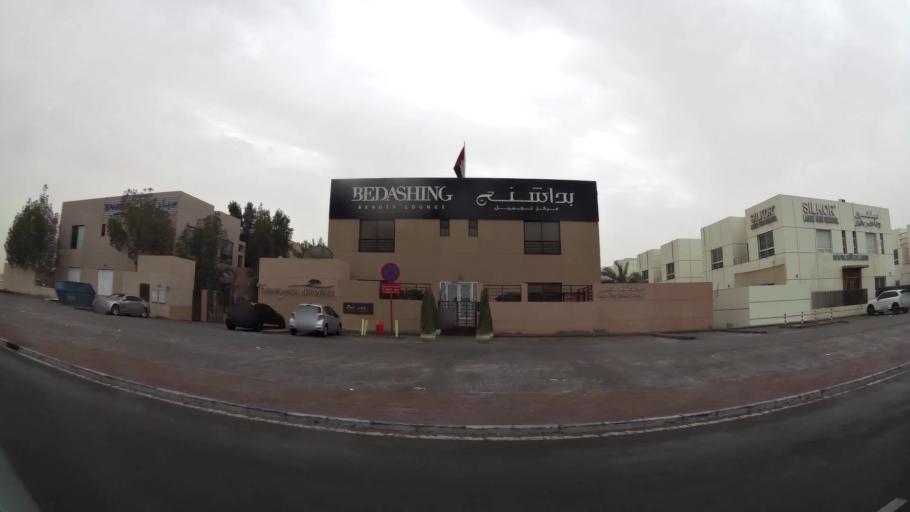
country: AE
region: Abu Dhabi
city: Abu Dhabi
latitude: 24.4404
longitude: 54.5996
